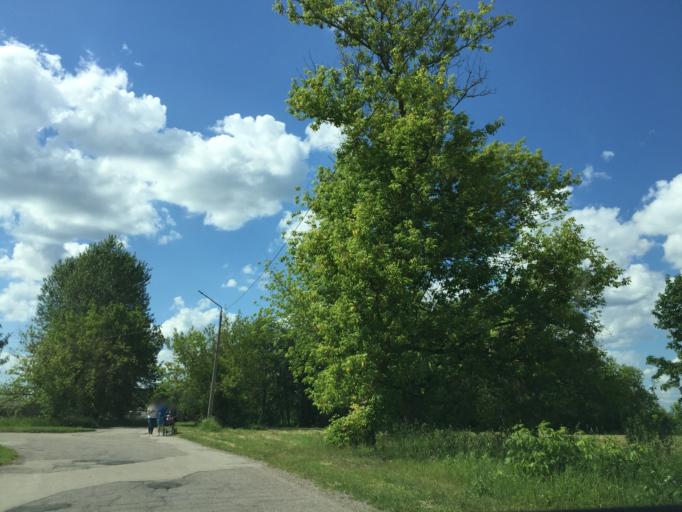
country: LV
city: Tireli
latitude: 56.8045
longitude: 23.5971
